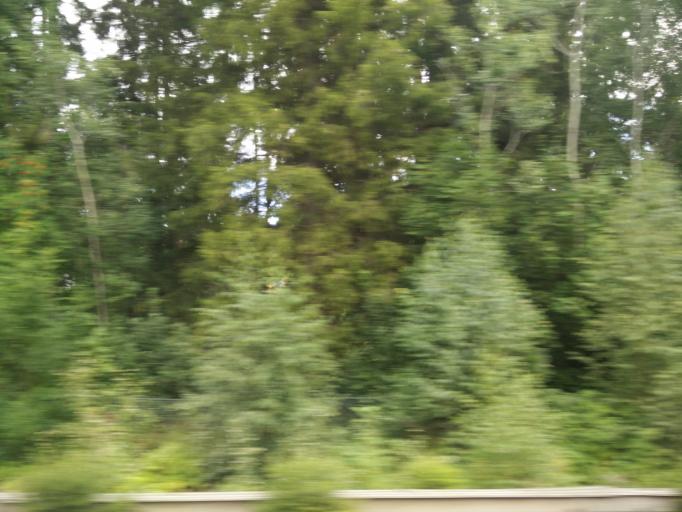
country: NO
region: Oslo
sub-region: Oslo
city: Sjolyststranda
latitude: 59.9450
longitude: 10.6697
